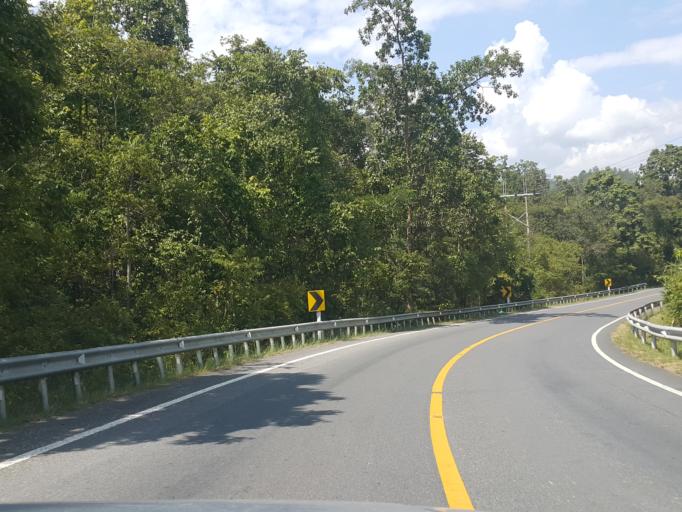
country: TH
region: Chiang Mai
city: Chom Thong
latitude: 18.5204
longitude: 98.6538
